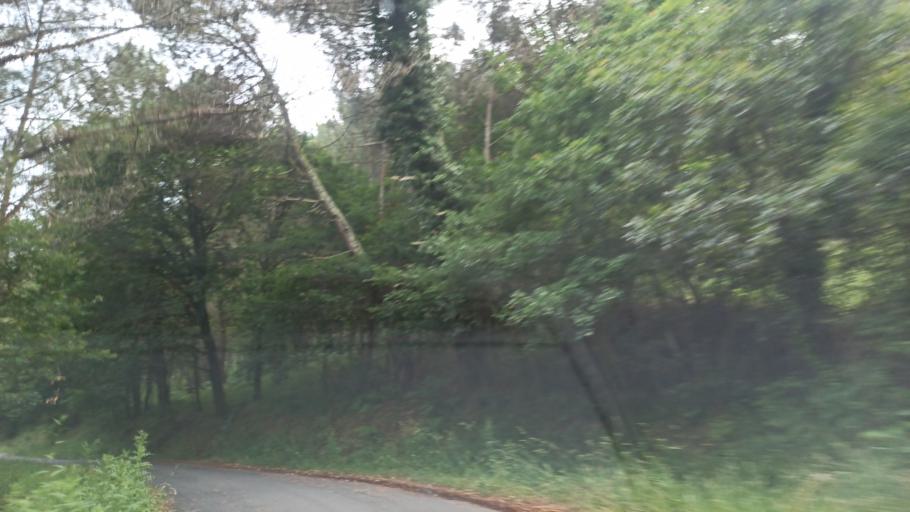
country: ES
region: Galicia
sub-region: Provincia da Coruna
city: Santiso
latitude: 42.8227
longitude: -8.1392
